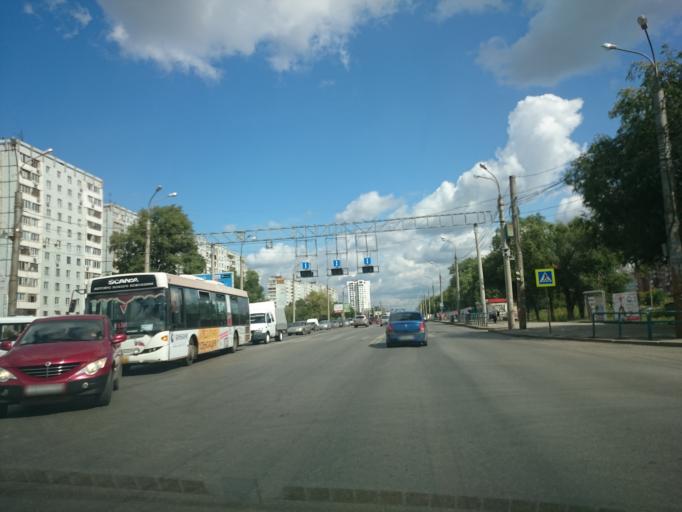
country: RU
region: Samara
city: Samara
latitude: 53.2557
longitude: 50.2302
